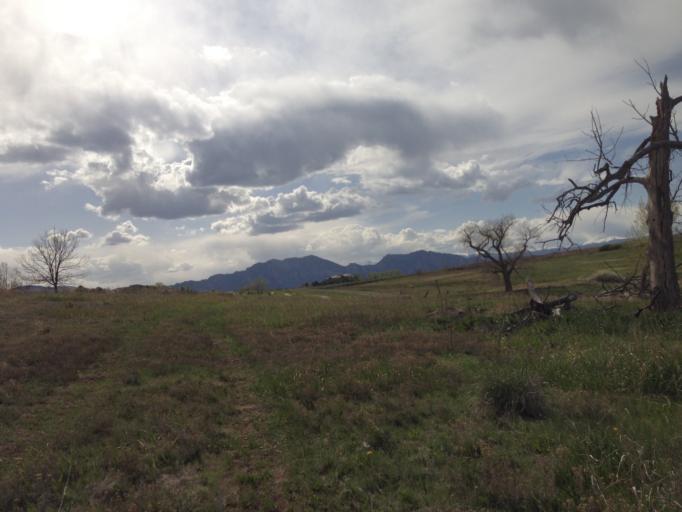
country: US
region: Colorado
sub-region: Boulder County
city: Superior
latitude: 39.9473
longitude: -105.1519
